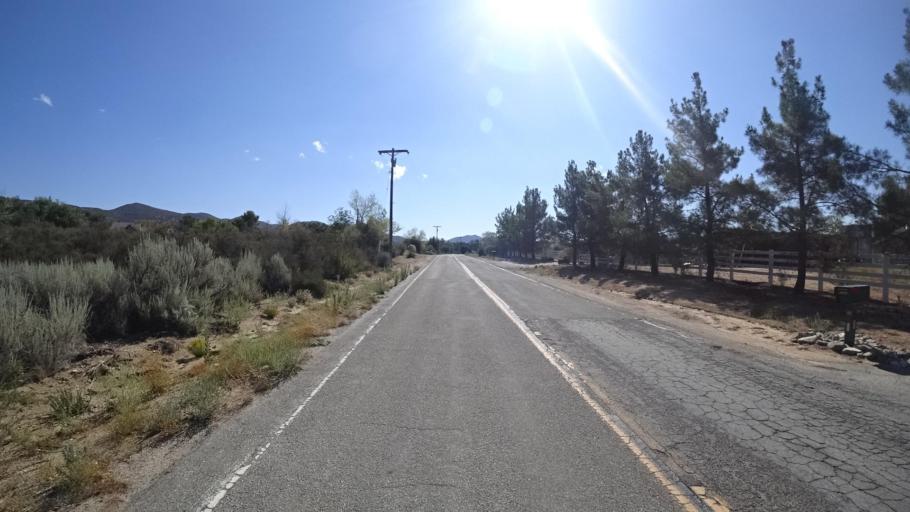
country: US
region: California
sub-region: Riverside County
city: Anza
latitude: 33.3860
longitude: -116.6642
